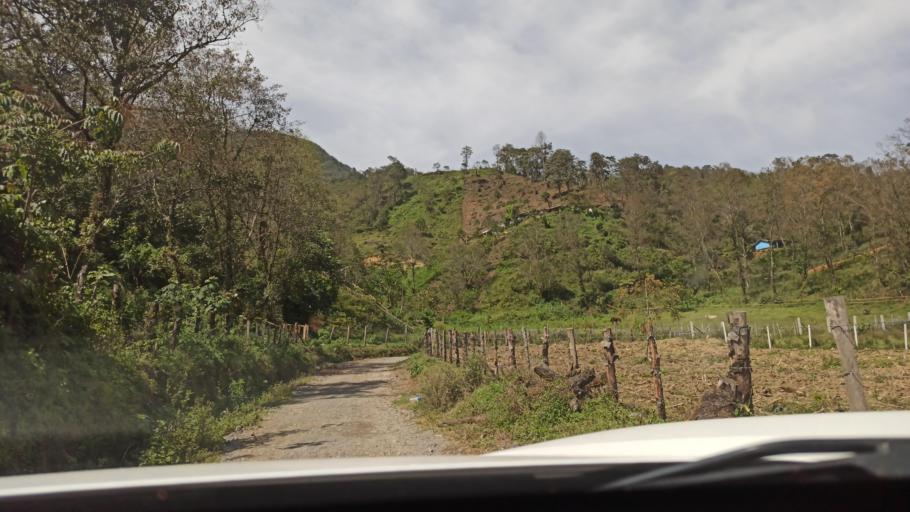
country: MX
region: Veracruz
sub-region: La Perla
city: Metlac Hernandez (Metlac Primero)
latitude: 18.9749
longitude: -97.1067
